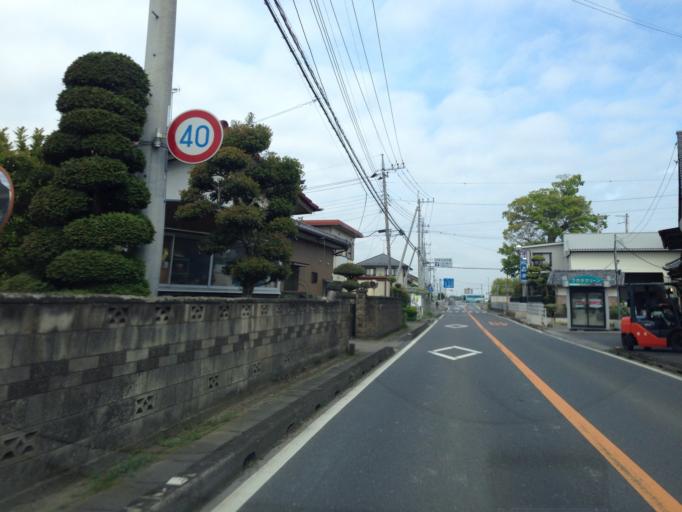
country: JP
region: Ibaraki
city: Ishige
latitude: 36.1496
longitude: 139.9951
